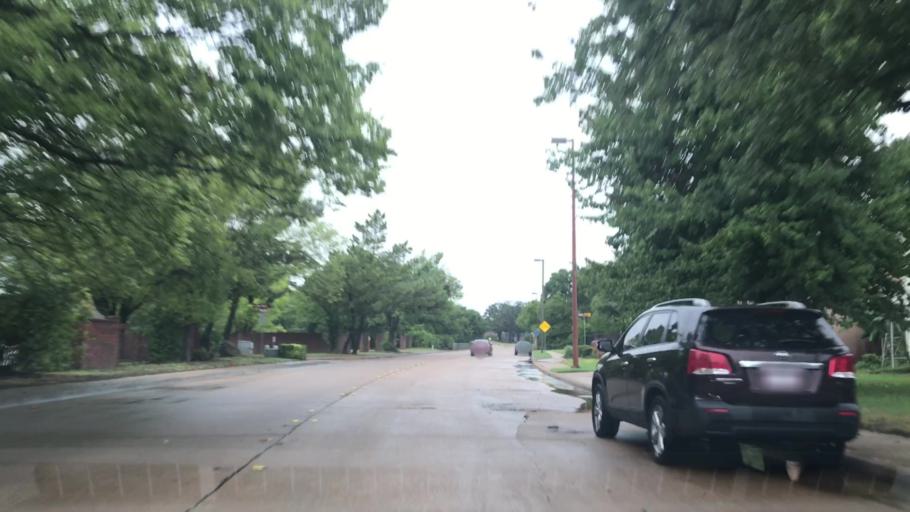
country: US
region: Texas
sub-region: Denton County
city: Highland Village
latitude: 33.0421
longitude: -97.0516
